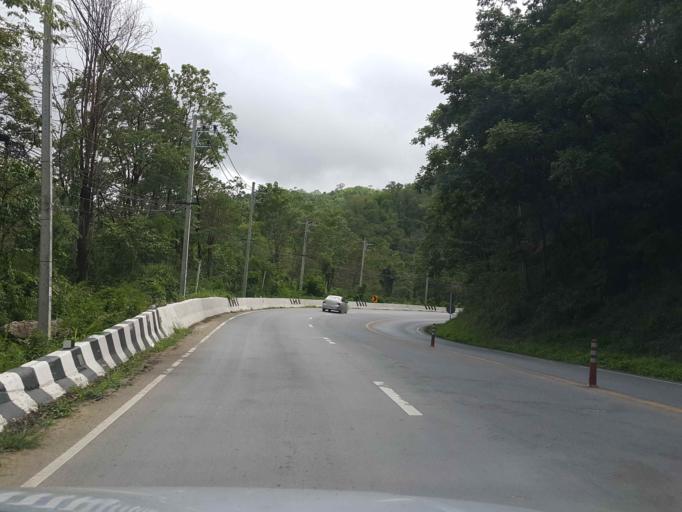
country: TH
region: Tak
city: Tak
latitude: 16.8128
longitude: 98.9650
